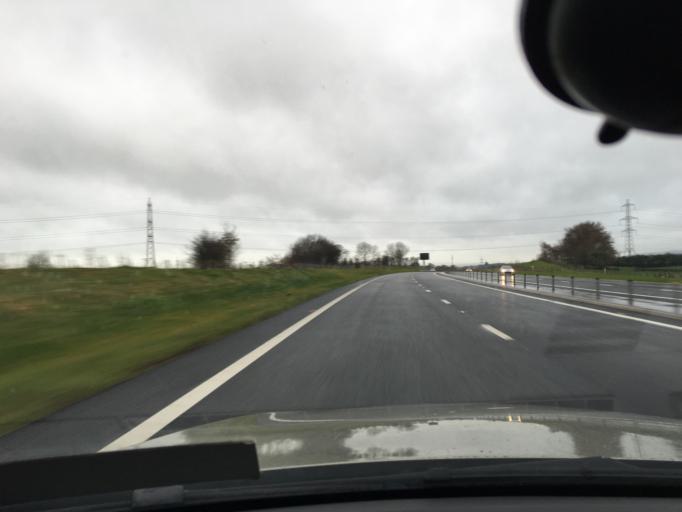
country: GB
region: Northern Ireland
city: Ballyclare
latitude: 54.7866
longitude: -5.9410
